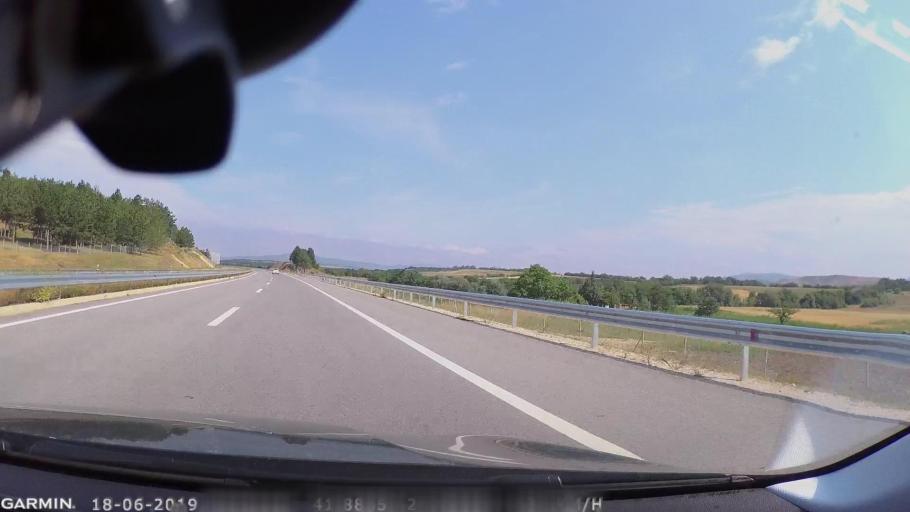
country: MK
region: Sveti Nikole
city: Sveti Nikole
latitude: 41.8874
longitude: 21.9319
